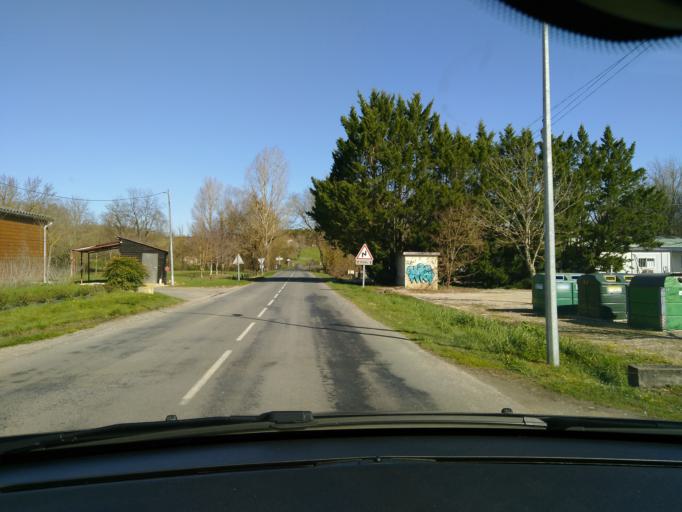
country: FR
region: Aquitaine
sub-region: Departement du Lot-et-Garonne
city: Saint-Hilaire
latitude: 44.5396
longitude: 0.6891
